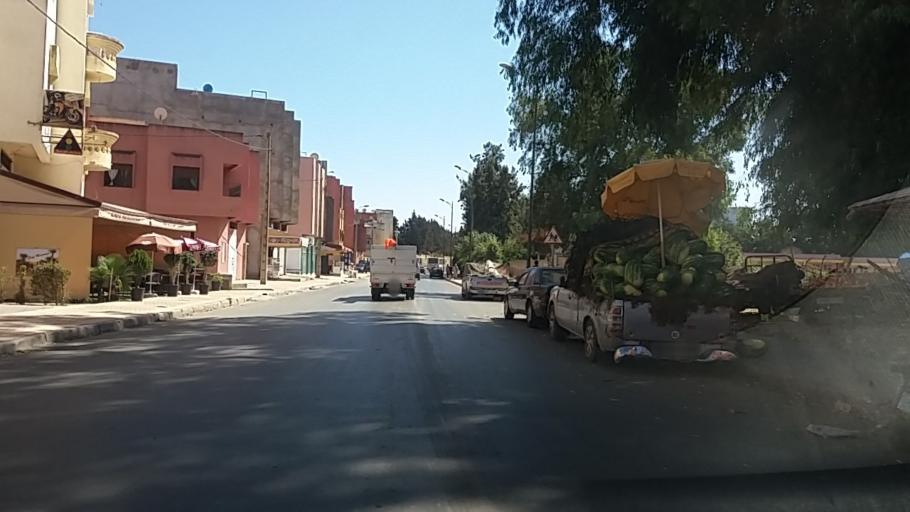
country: MA
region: Gharb-Chrarda-Beni Hssen
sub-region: Kenitra Province
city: Kenitra
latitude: 34.2432
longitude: -6.6136
